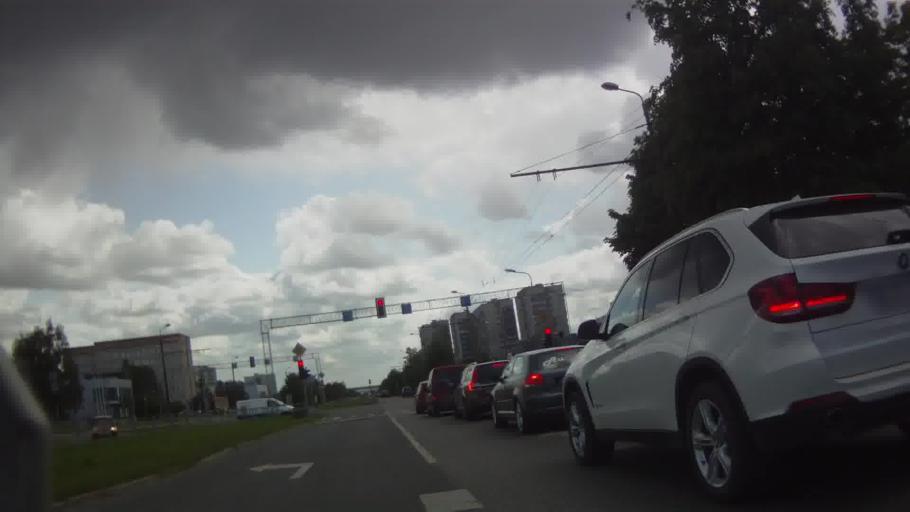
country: LV
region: Stopini
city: Ulbroka
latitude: 56.9404
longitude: 24.2042
